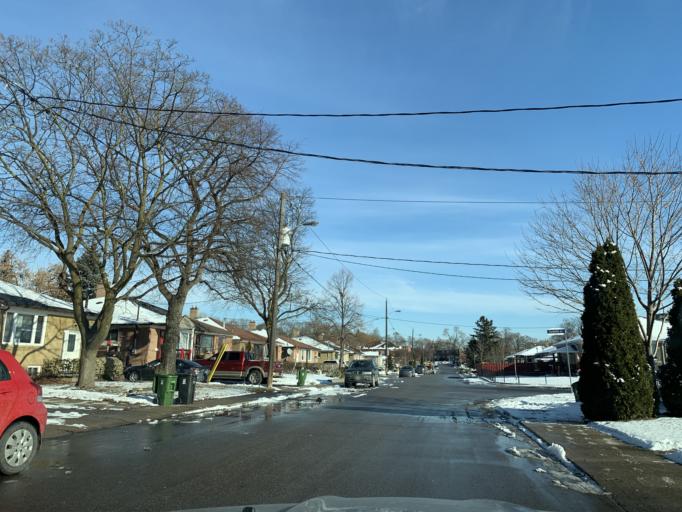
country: CA
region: Ontario
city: Toronto
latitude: 43.6800
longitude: -79.4876
